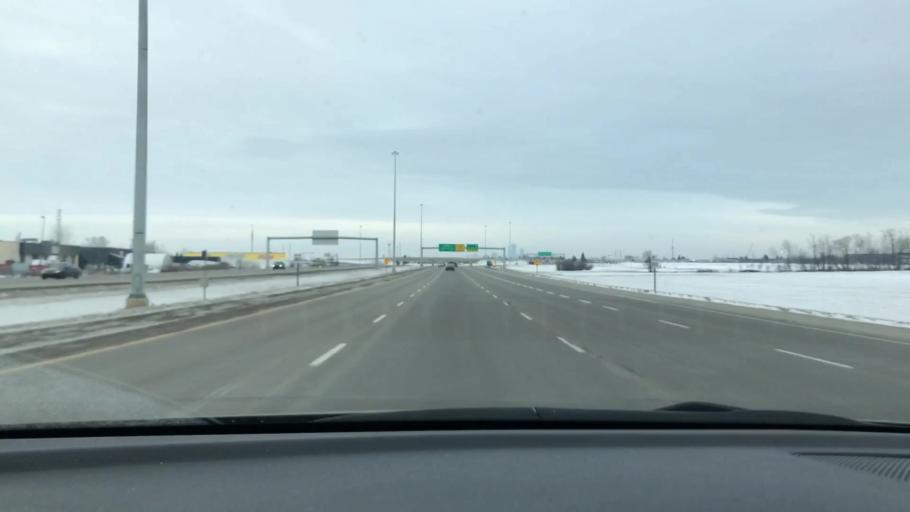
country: CA
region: Alberta
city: Sherwood Park
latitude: 53.5153
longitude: -113.3573
